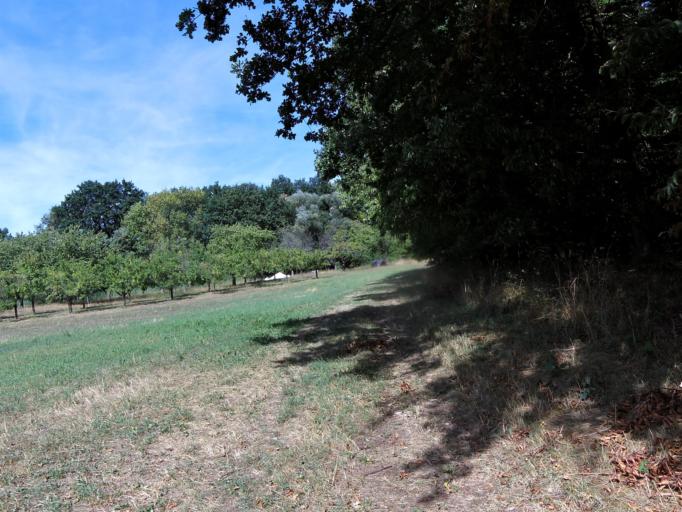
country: DE
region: Bavaria
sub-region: Regierungsbezirk Unterfranken
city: Eibelstadt
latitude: 49.7449
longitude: 10.0098
